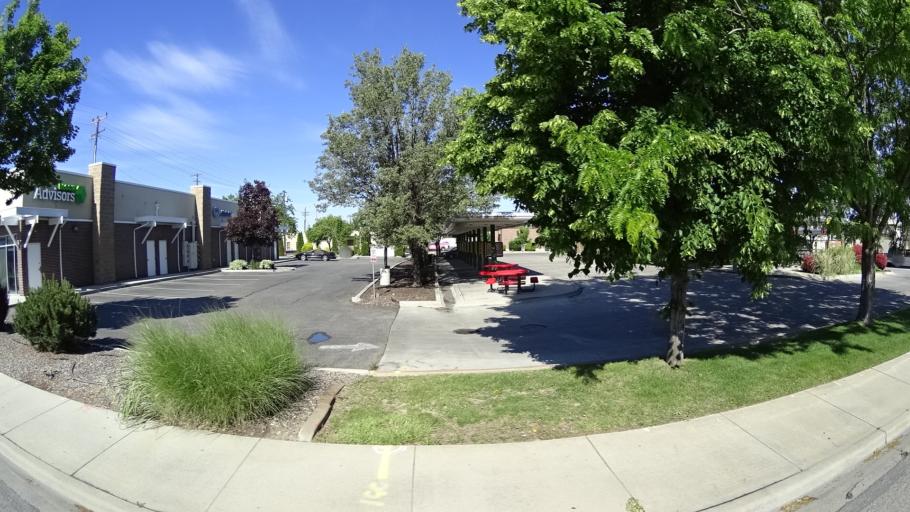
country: US
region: Idaho
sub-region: Ada County
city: Garden City
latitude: 43.6122
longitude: -116.2436
